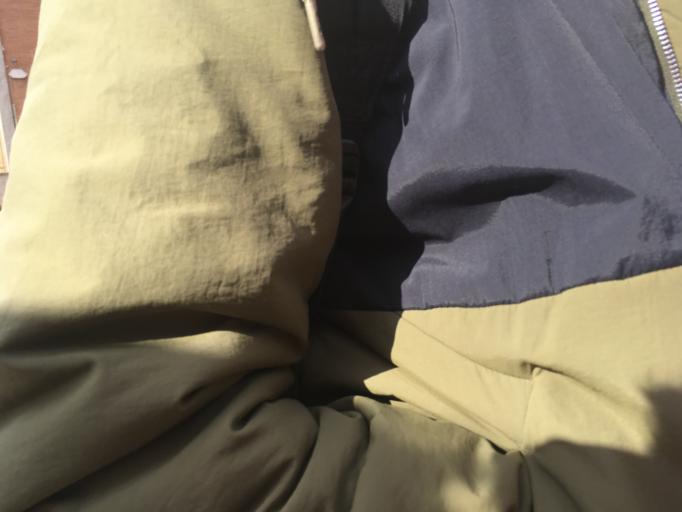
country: IT
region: Apulia
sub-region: Provincia di Bari
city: Bitonto
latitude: 41.1112
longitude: 16.6983
